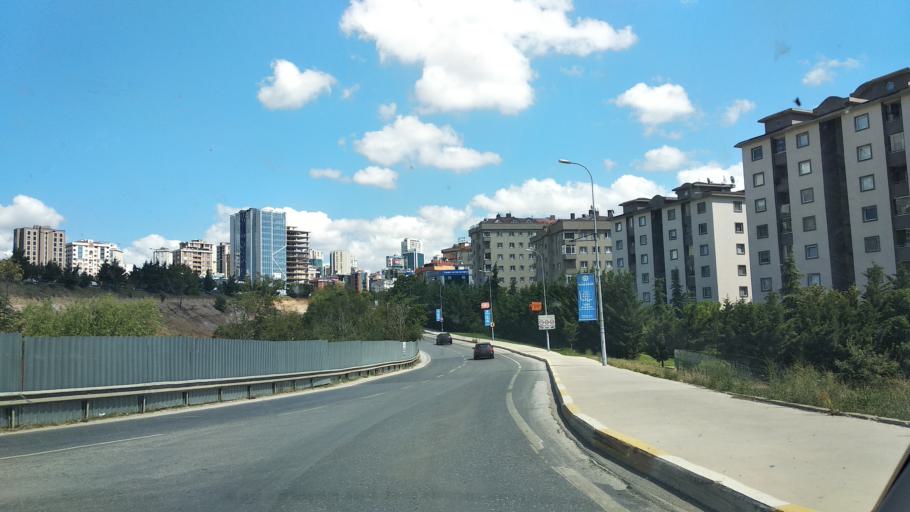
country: TR
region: Istanbul
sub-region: Atasehir
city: Atasehir
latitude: 40.9957
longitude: 29.1302
